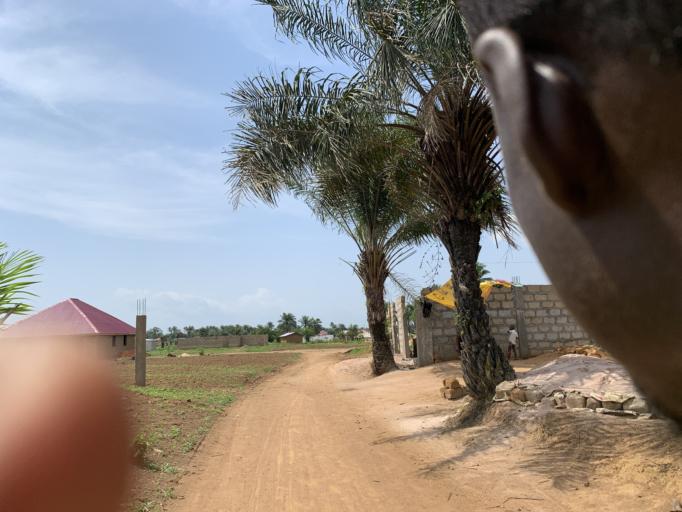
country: SL
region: Western Area
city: Waterloo
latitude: 8.3554
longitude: -13.0450
